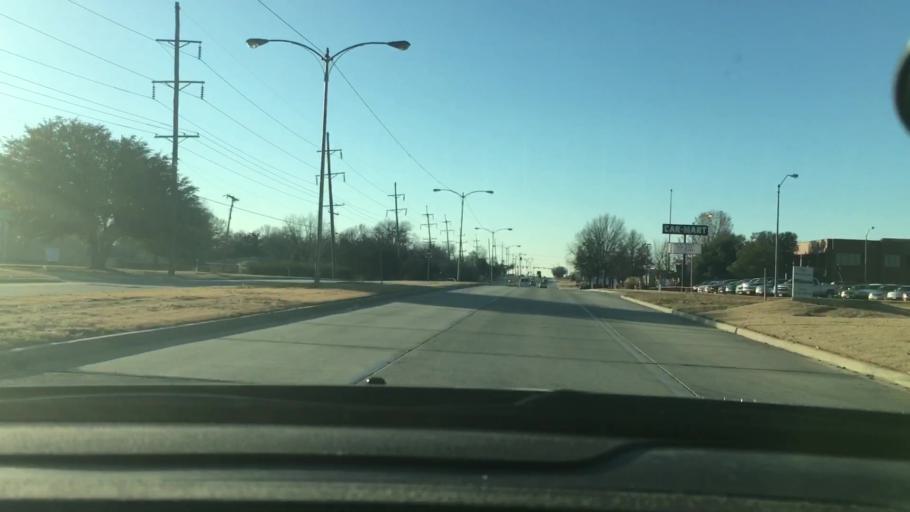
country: US
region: Oklahoma
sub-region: Carter County
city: Ardmore
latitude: 34.1984
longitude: -97.1432
